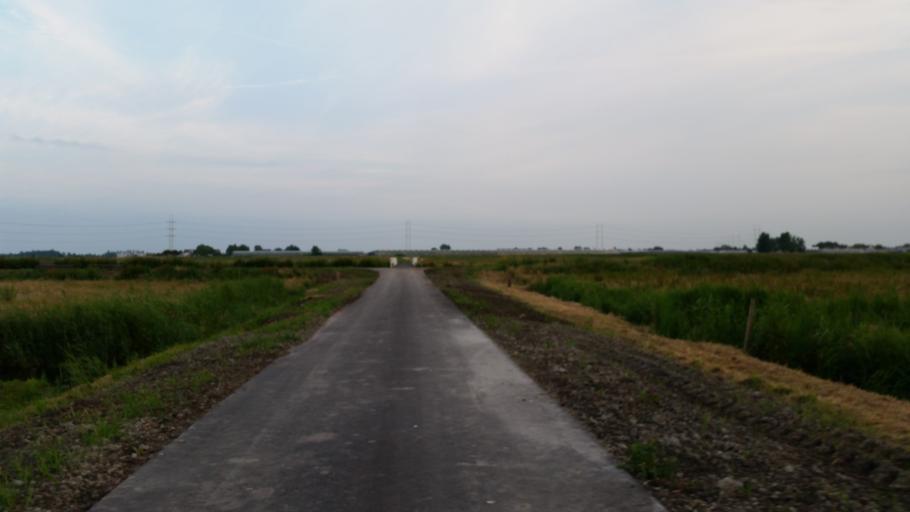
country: NL
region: South Holland
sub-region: Gemeente Pijnacker-Nootdorp
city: Pijnacker
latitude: 52.0345
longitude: 4.4605
